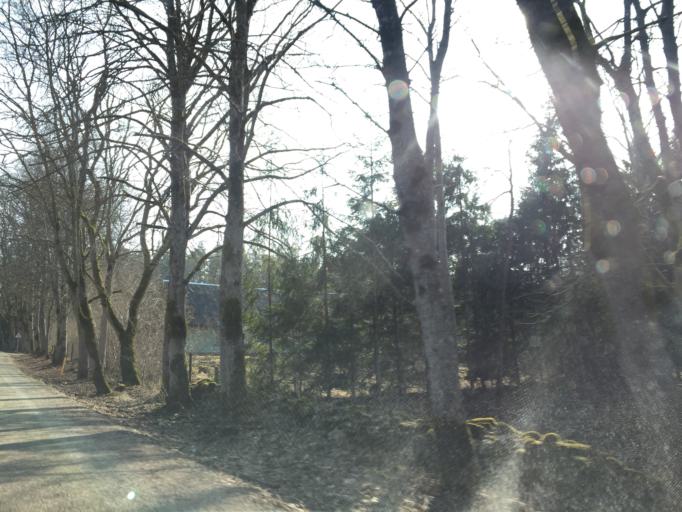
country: EE
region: Saare
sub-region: Orissaare vald
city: Orissaare
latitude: 58.5541
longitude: 23.2777
